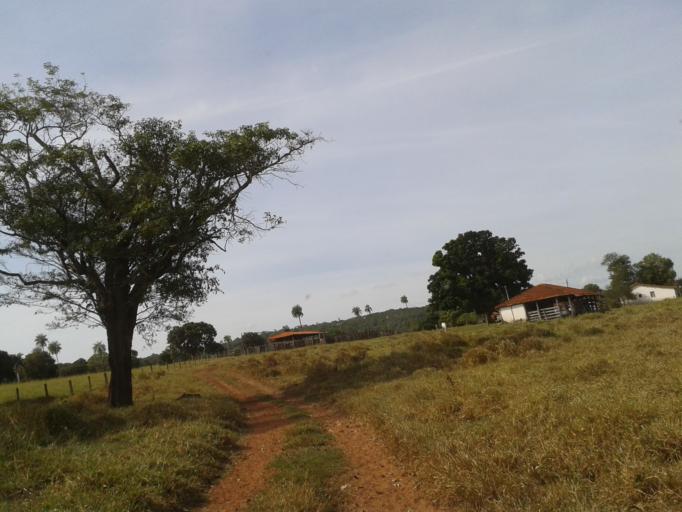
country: BR
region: Minas Gerais
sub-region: Campina Verde
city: Campina Verde
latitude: -19.4976
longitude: -49.5867
